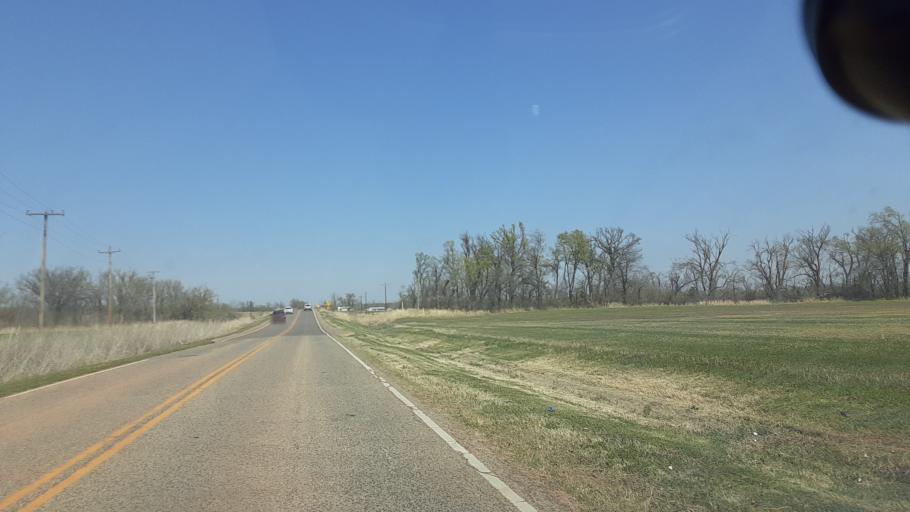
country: US
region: Oklahoma
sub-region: Logan County
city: Guthrie
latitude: 35.8114
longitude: -97.4784
